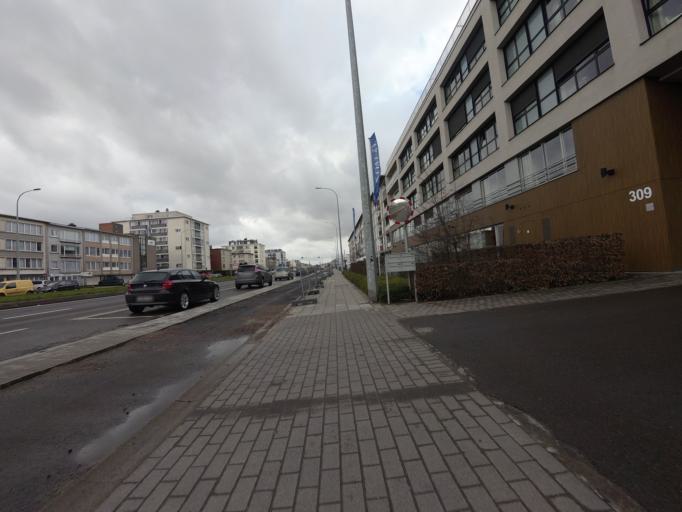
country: BE
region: Flanders
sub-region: Provincie Antwerpen
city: Borsbeek
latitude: 51.2335
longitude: 4.4619
